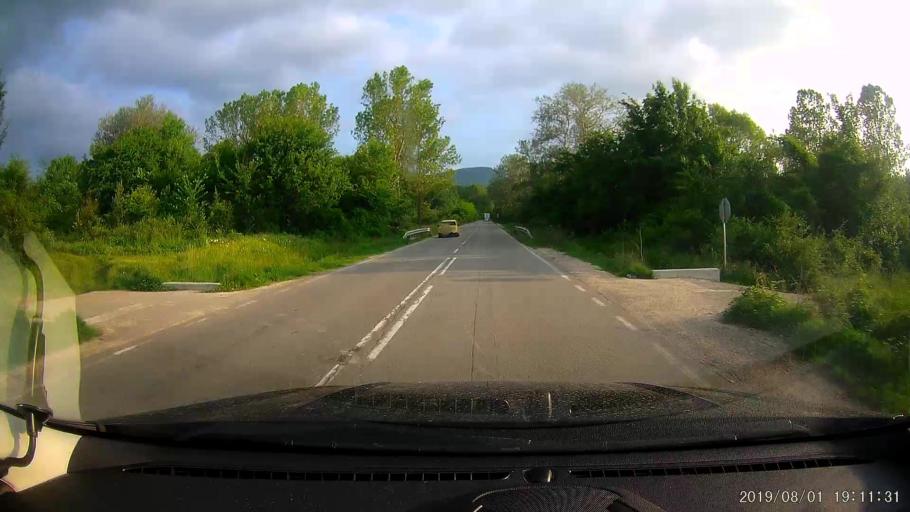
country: BG
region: Shumen
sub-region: Obshtina Smyadovo
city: Smyadovo
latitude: 42.9733
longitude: 26.9603
